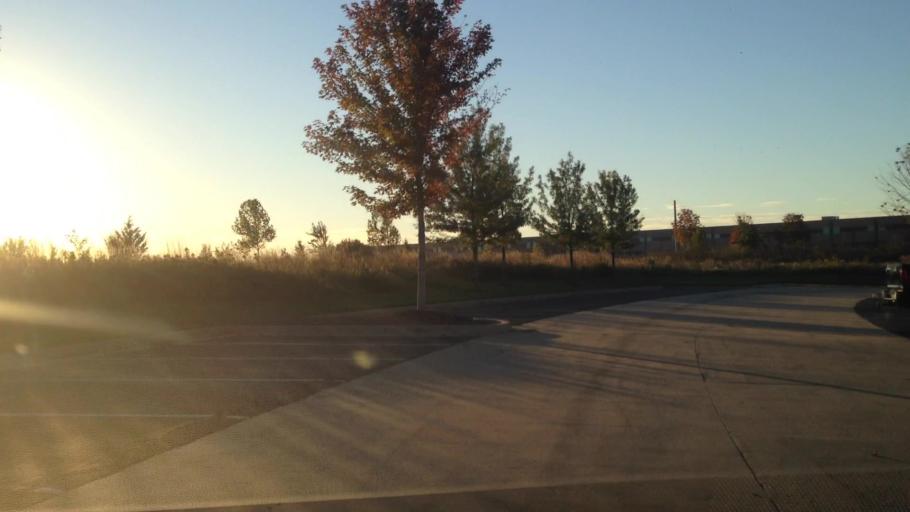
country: US
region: Kansas
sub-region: Johnson County
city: Olathe
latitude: 38.9339
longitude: -94.7942
